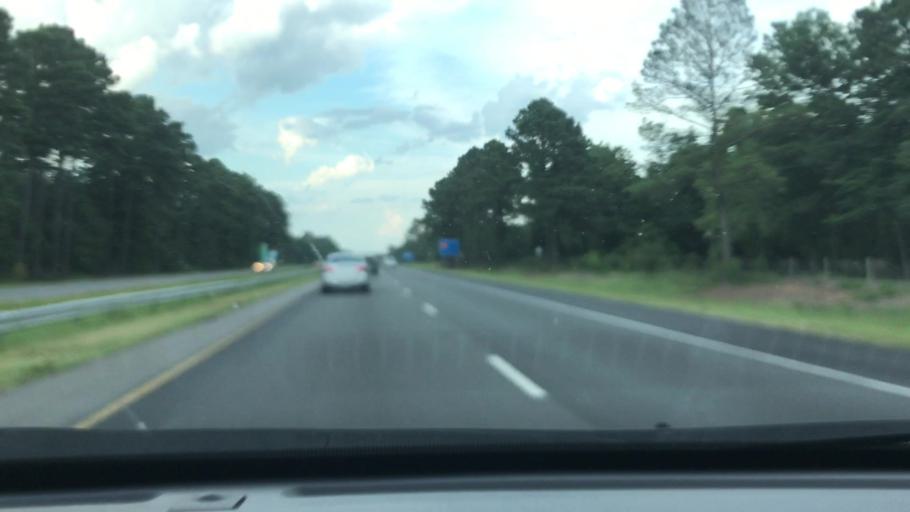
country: US
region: North Carolina
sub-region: Cumberland County
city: Eastover
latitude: 35.1131
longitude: -78.7648
